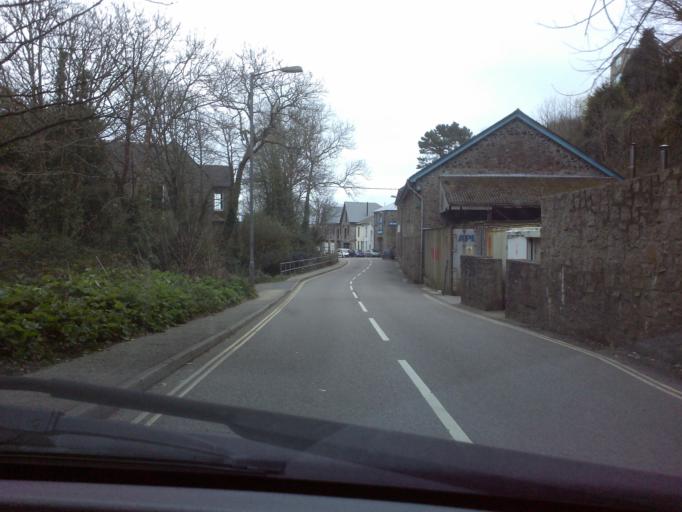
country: GB
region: England
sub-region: Cornwall
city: Penzance
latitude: 50.1077
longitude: -5.5529
